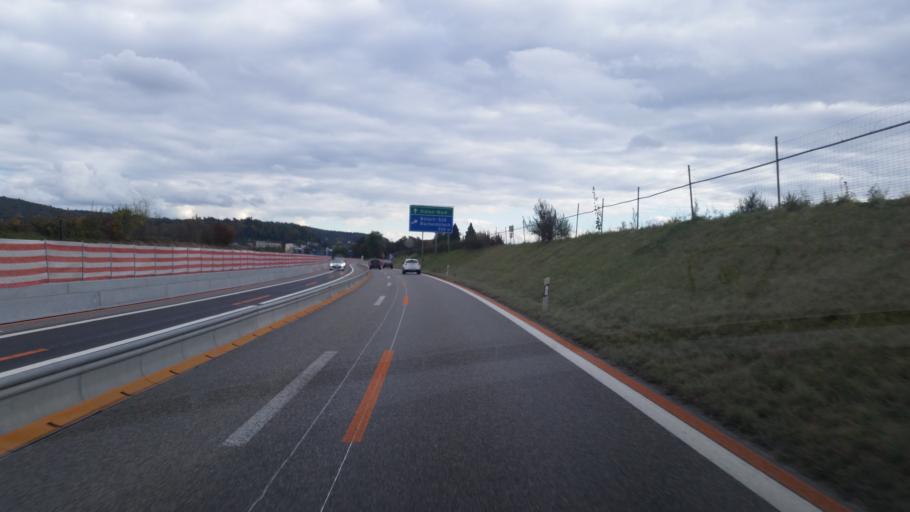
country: CH
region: Zurich
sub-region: Bezirk Buelach
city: Buelach / Niederflachs
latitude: 47.5100
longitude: 8.5287
